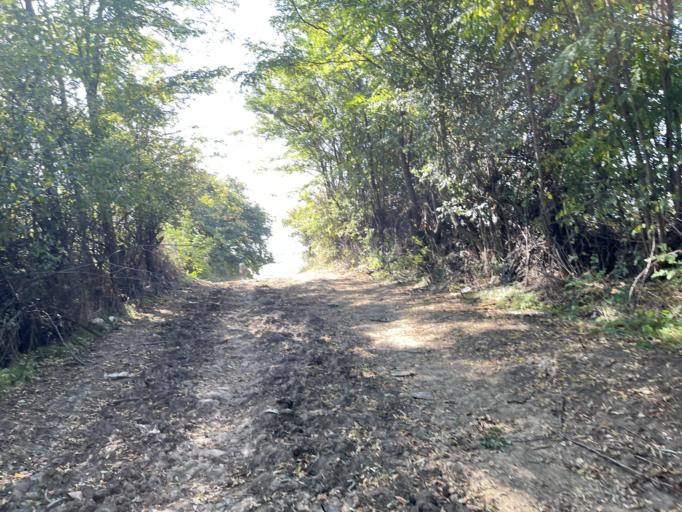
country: RO
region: Iasi
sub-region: Comuna Dumesti
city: Pausesti
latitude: 47.1559
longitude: 27.3137
